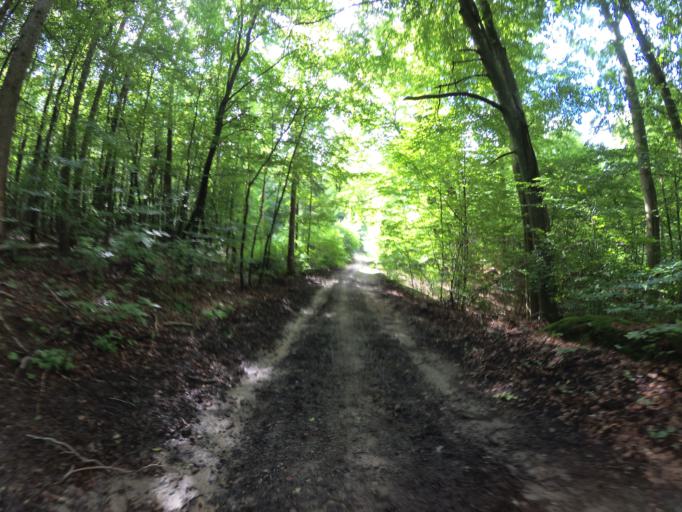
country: PL
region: Pomeranian Voivodeship
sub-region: Gdynia
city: Wielki Kack
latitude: 54.5065
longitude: 18.4487
